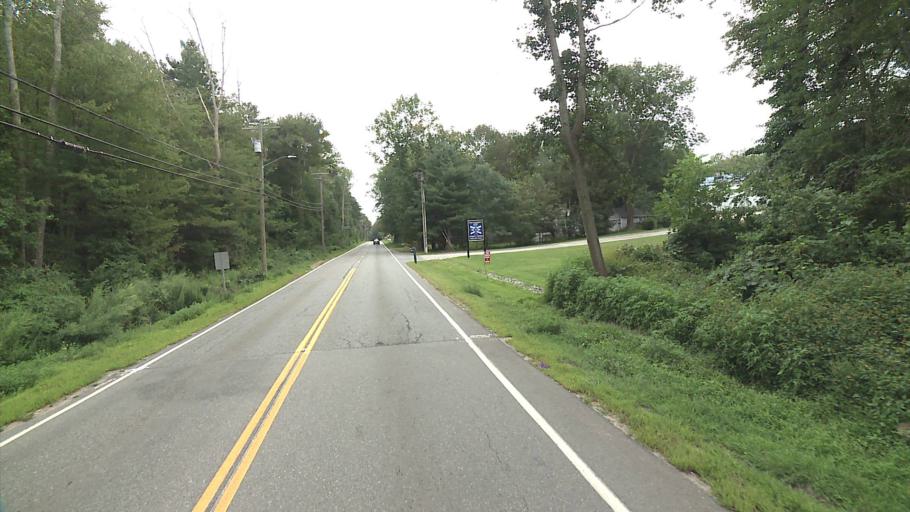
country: US
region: Connecticut
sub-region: New London County
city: Montville Center
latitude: 41.4234
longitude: -72.2044
